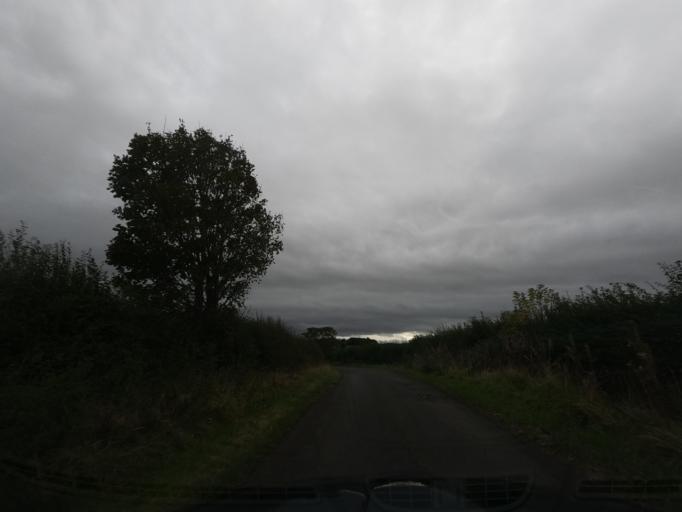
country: GB
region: England
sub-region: Northumberland
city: Ford
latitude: 55.7036
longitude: -2.0868
